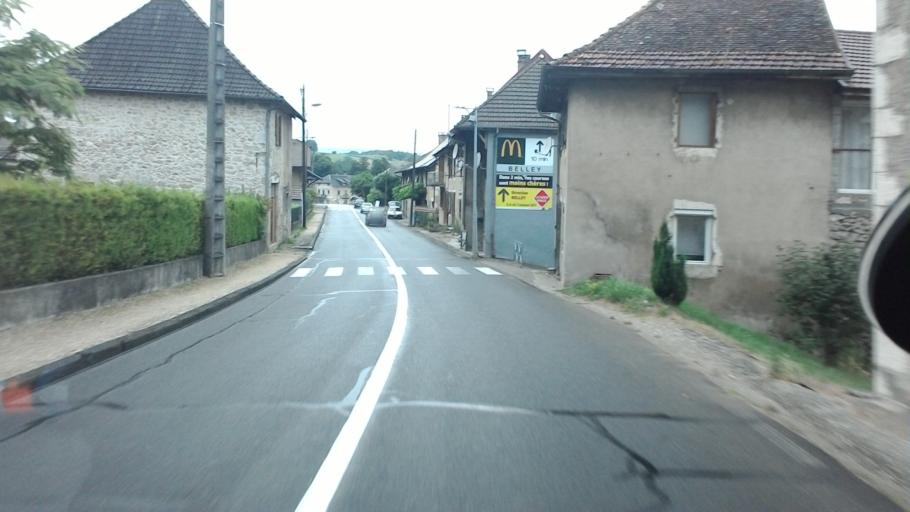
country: FR
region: Rhone-Alpes
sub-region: Departement de la Savoie
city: Le Bourget-du-Lac
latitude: 45.6906
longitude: 5.8185
